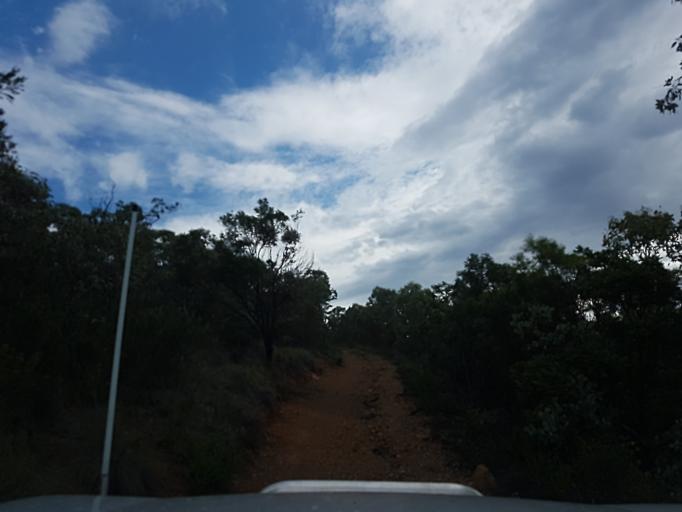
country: AU
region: New South Wales
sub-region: Snowy River
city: Jindabyne
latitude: -36.9963
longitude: 148.4061
